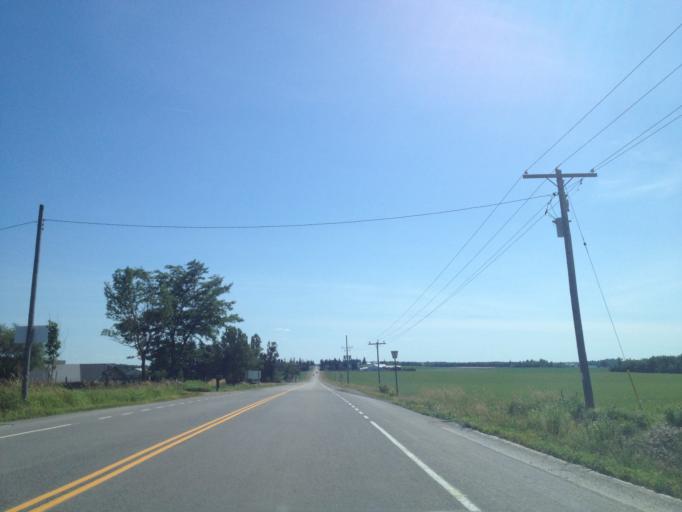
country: CA
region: Ontario
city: Waterloo
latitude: 43.5276
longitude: -80.7440
